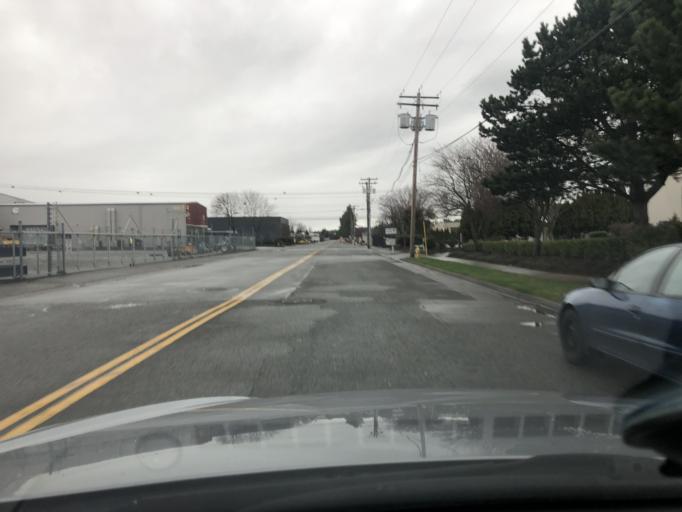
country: US
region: Washington
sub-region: King County
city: Auburn
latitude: 47.3349
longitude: -122.2265
